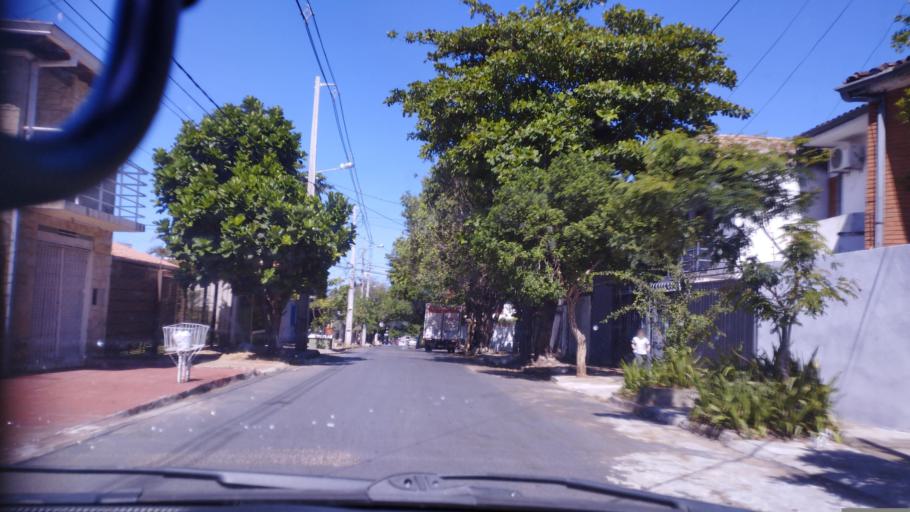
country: PY
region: Asuncion
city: Asuncion
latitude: -25.2958
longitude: -57.6631
